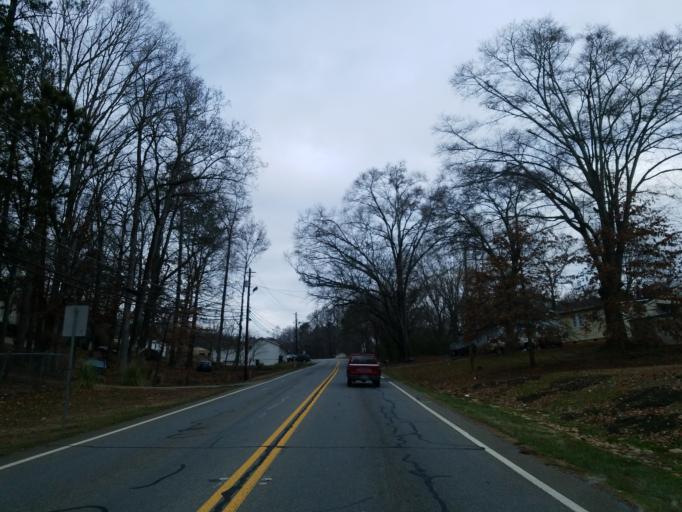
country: US
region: Georgia
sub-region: Cherokee County
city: Canton
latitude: 34.2510
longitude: -84.4939
